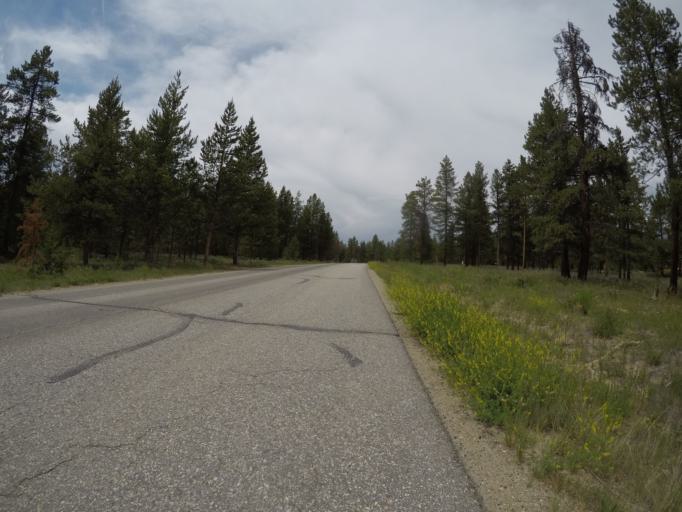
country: US
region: Colorado
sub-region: Grand County
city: Fraser
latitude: 39.9913
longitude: -105.8910
